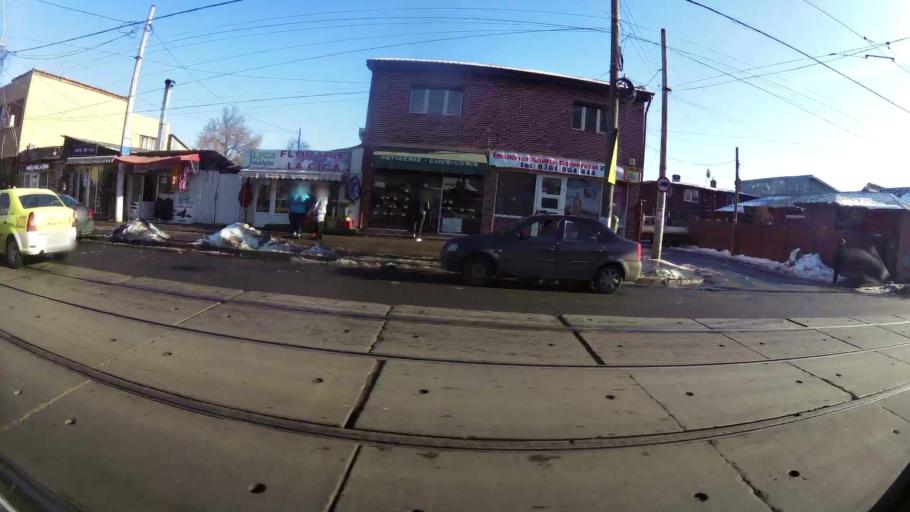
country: RO
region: Bucuresti
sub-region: Municipiul Bucuresti
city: Bucuresti
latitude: 44.3897
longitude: 26.0804
